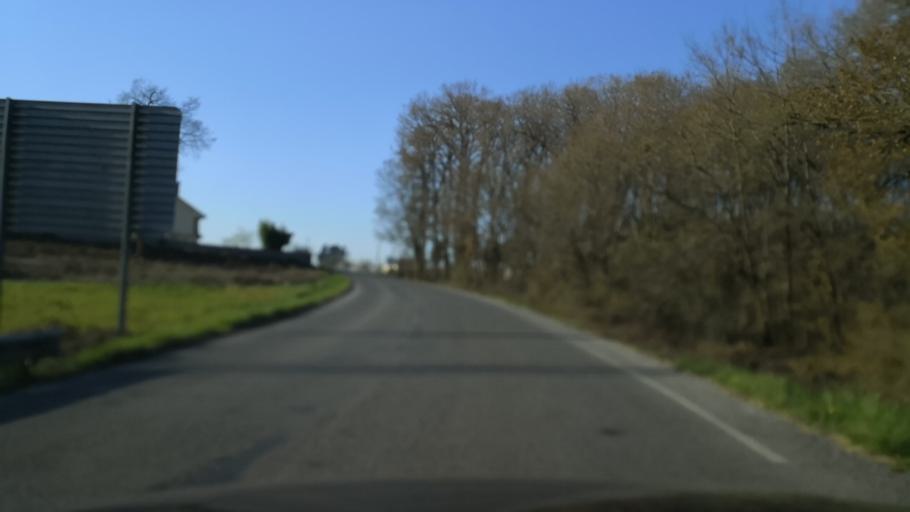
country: ES
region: Galicia
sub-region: Provincia de Lugo
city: Corgo
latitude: 42.9341
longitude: -7.3980
